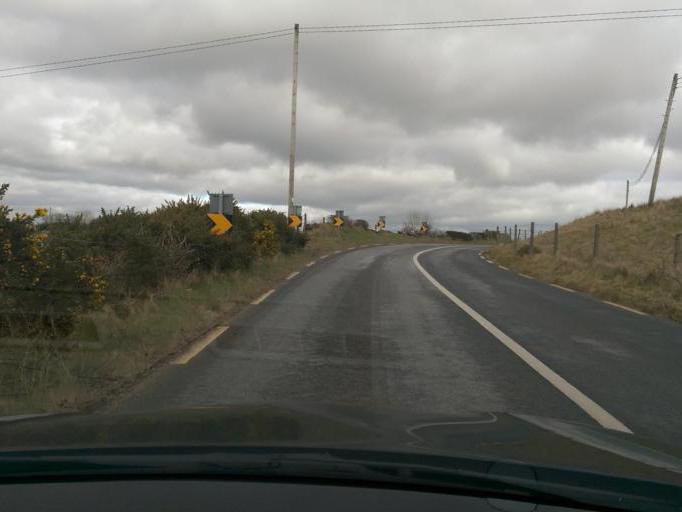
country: IE
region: Connaught
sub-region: County Galway
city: Loughrea
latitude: 53.3235
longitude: -8.4312
